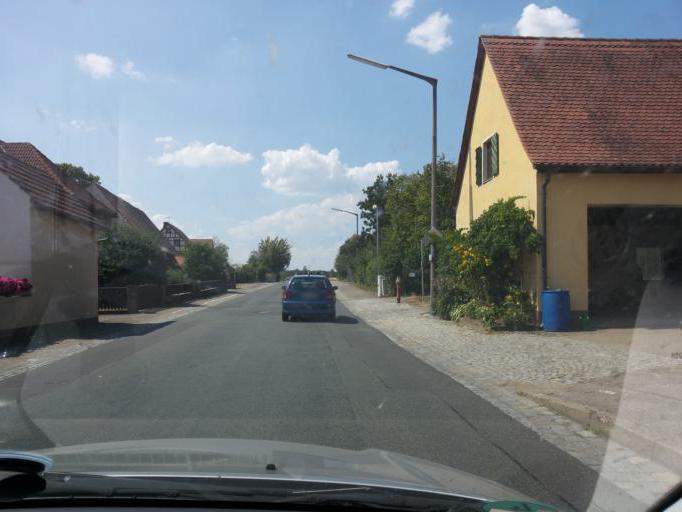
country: DE
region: Bavaria
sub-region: Regierungsbezirk Mittelfranken
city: Trautskirchen
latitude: 49.4998
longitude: 10.5807
